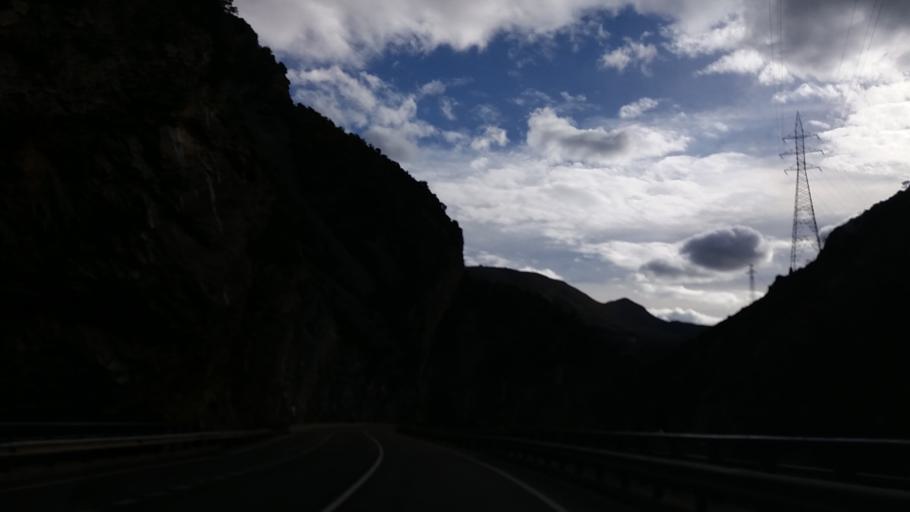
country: ES
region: Aragon
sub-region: Provincia de Huesca
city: Arguis
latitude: 42.3006
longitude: -0.4285
